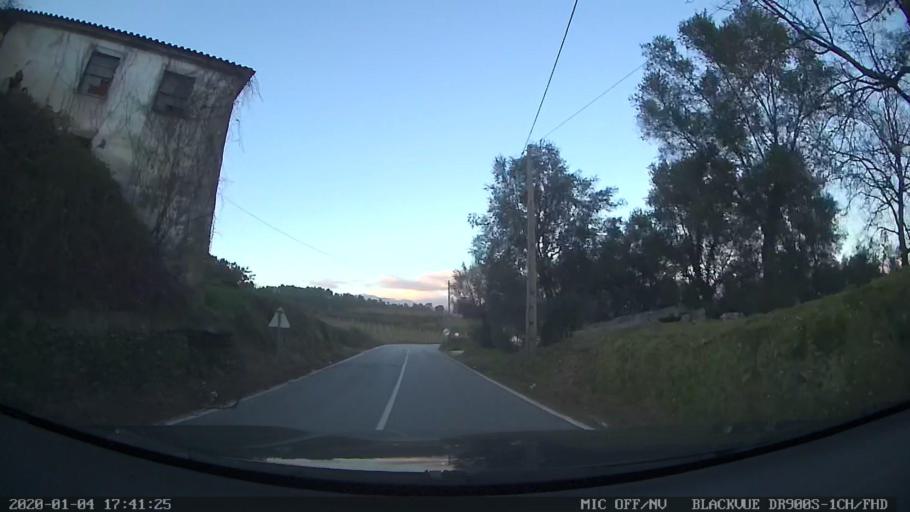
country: PT
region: Vila Real
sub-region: Mondim de Basto
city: Mondim de Basto
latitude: 41.4659
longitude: -7.9547
